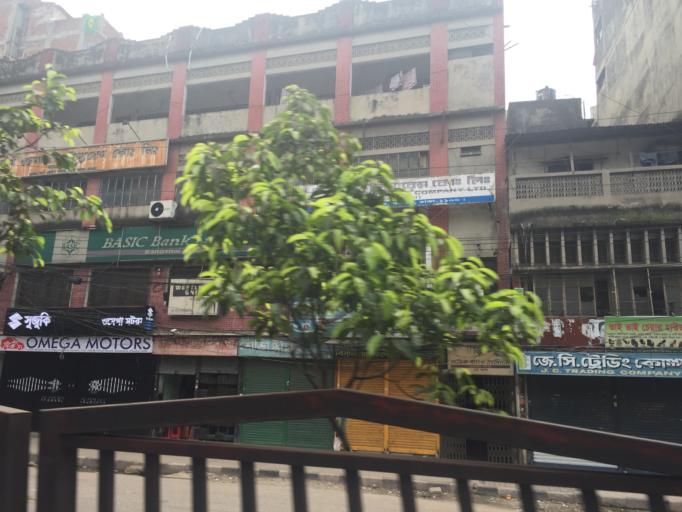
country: BD
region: Dhaka
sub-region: Dhaka
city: Dhaka
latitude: 23.7178
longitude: 90.4088
